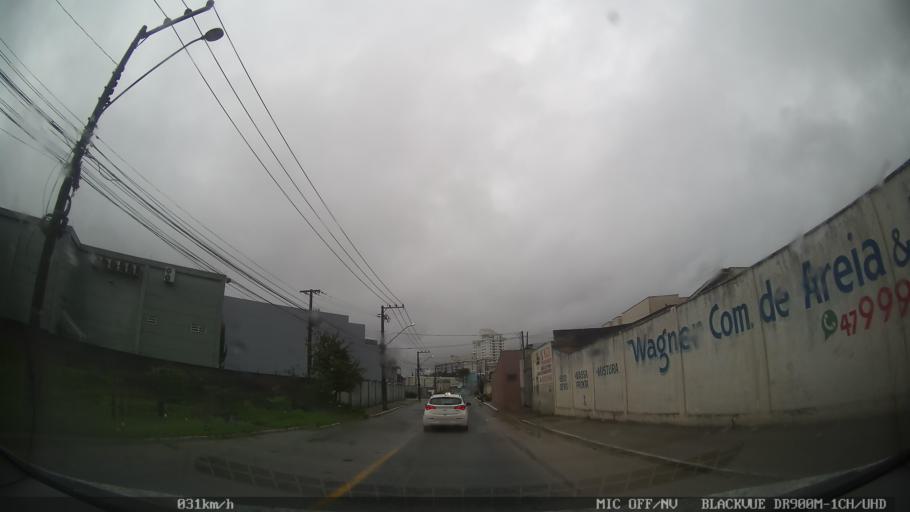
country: BR
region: Santa Catarina
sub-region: Itajai
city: Itajai
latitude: -26.9288
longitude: -48.6852
